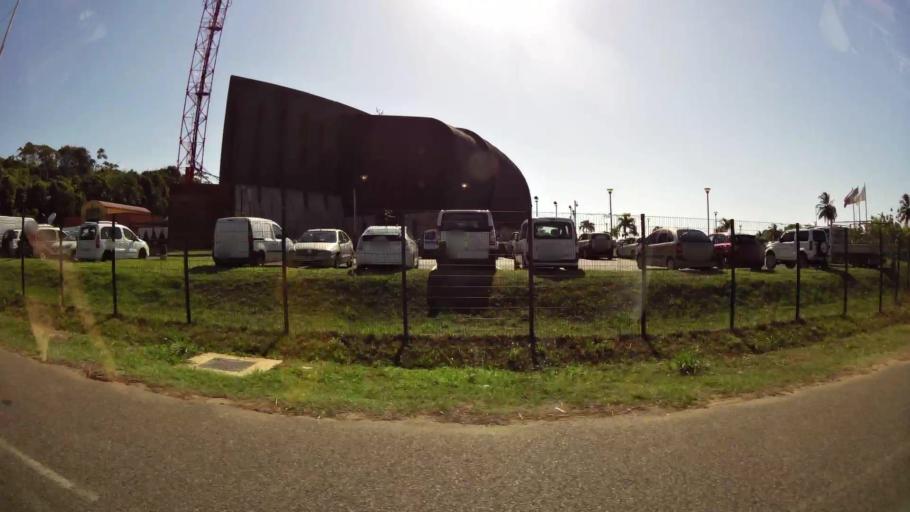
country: GF
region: Guyane
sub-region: Guyane
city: Remire-Montjoly
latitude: 4.9040
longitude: -52.2734
